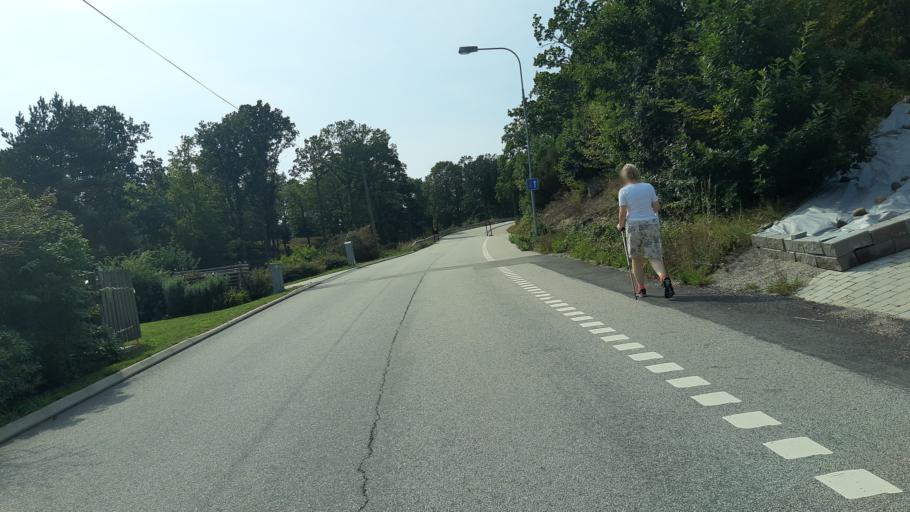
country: SE
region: Blekinge
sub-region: Ronneby Kommun
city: Ronneby
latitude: 56.1802
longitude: 15.2642
